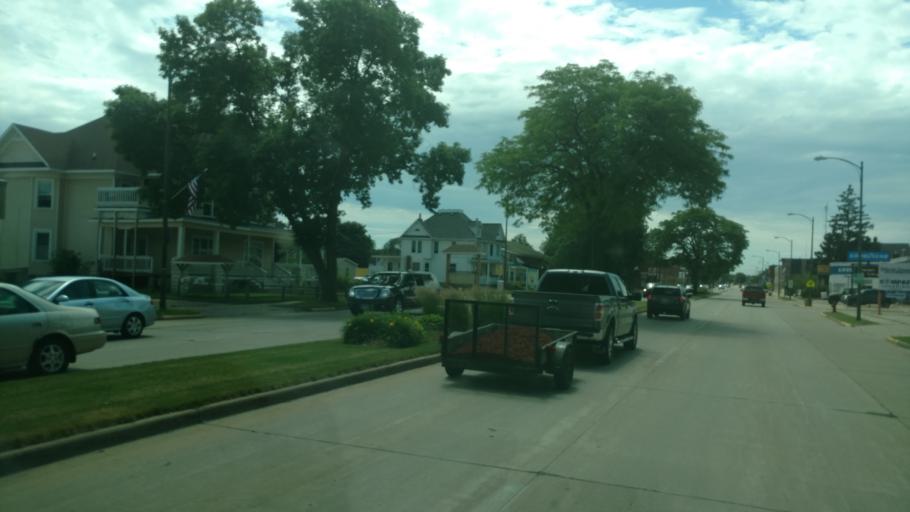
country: US
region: Wisconsin
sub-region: Monroe County
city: Tomah
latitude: 43.9812
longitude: -90.5048
